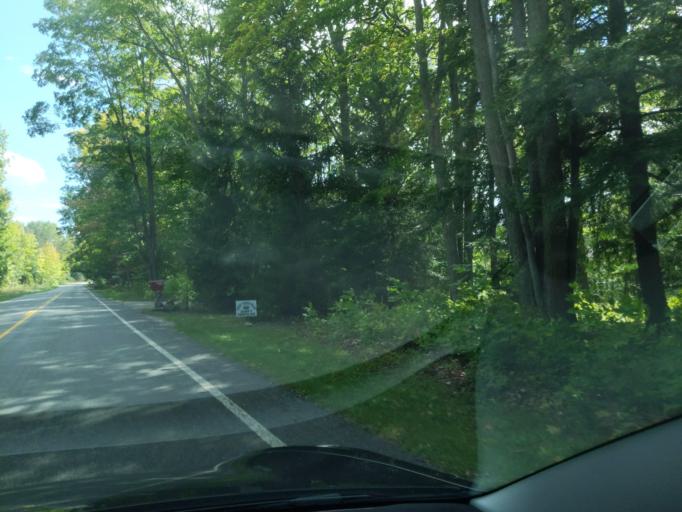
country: US
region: Michigan
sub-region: Antrim County
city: Bellaire
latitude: 44.9920
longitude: -85.2862
